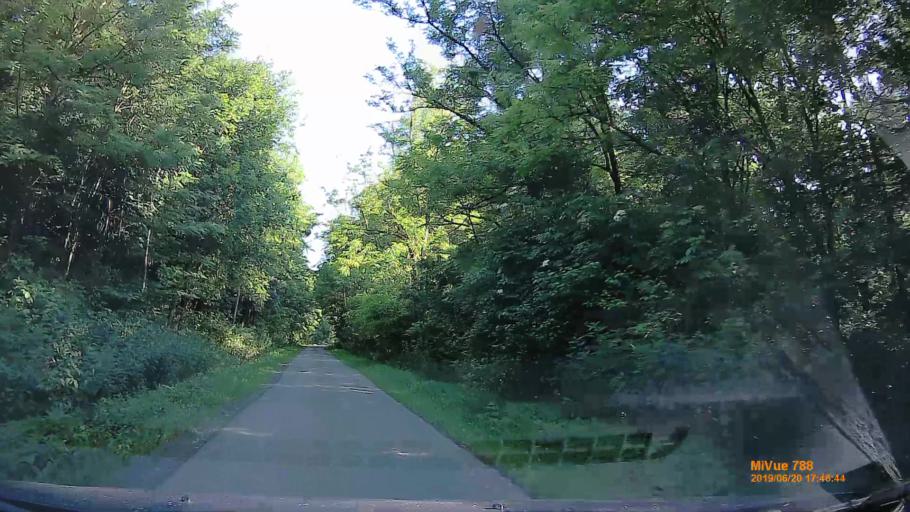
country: HU
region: Baranya
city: Buekkoesd
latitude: 46.1319
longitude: 18.0037
